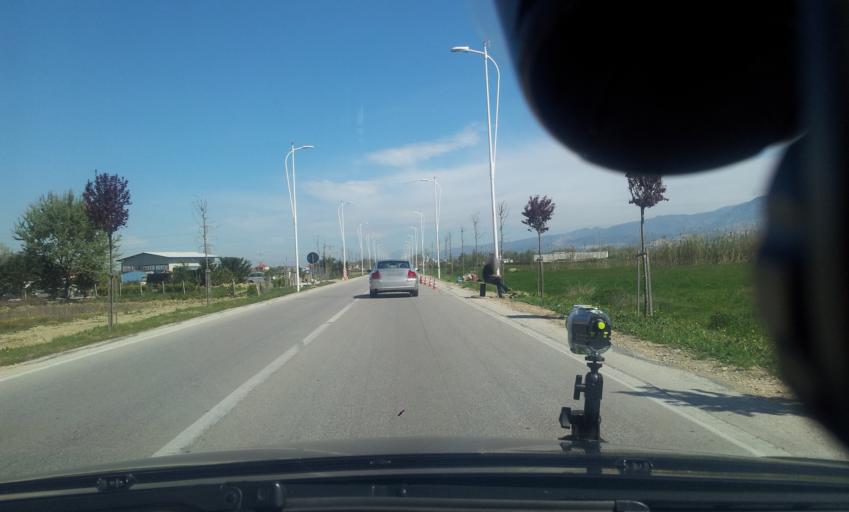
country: AL
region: Tirane
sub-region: Rrethi i Tiranes
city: Berxull
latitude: 41.3794
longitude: 19.7037
